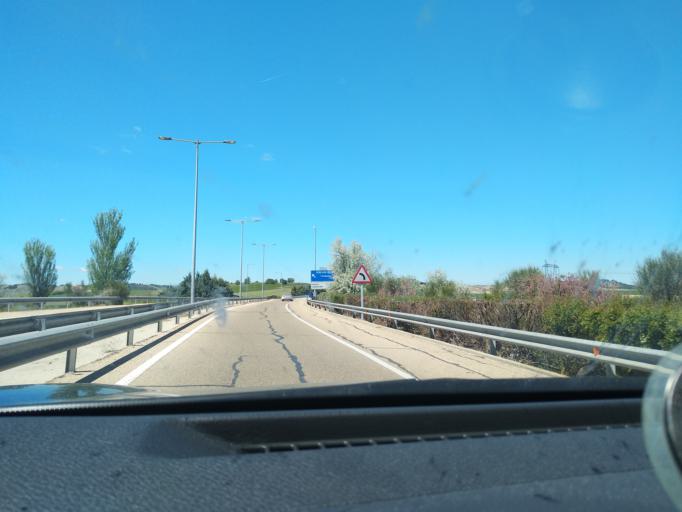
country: ES
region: Castille and Leon
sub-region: Provincia de Valladolid
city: Zaratan
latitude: 41.6434
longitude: -4.7662
